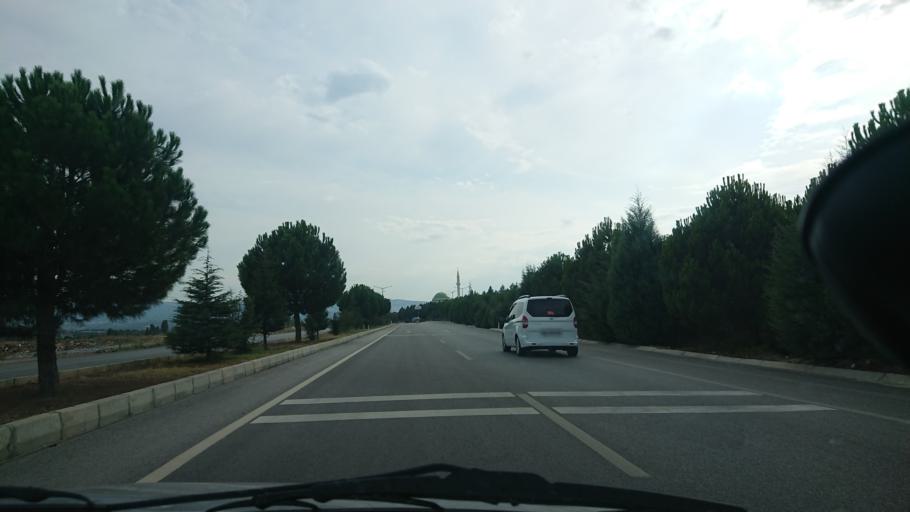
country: TR
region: Kuetahya
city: Gediz
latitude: 39.0082
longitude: 29.4071
